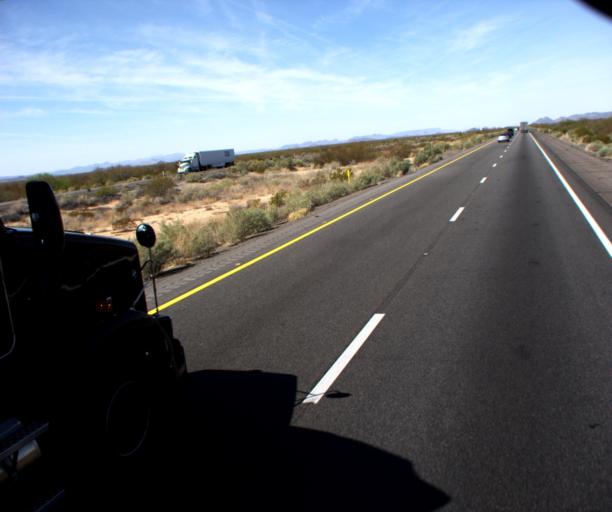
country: US
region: Arizona
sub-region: La Paz County
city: Salome
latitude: 33.5846
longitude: -113.4549
